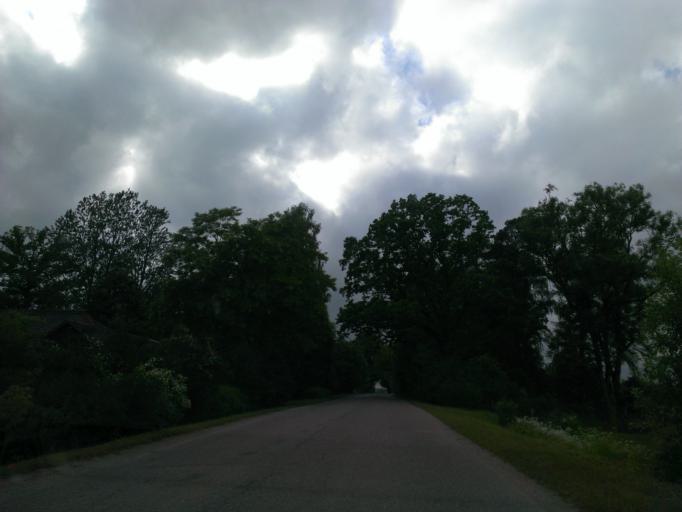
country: LV
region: Aizpute
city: Aizpute
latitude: 56.7124
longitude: 21.4791
